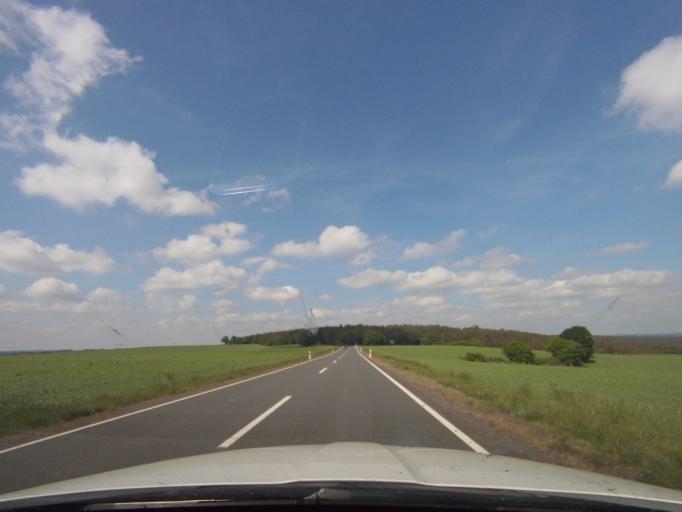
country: DE
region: Thuringia
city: Bocka
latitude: 50.8116
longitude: 11.9773
